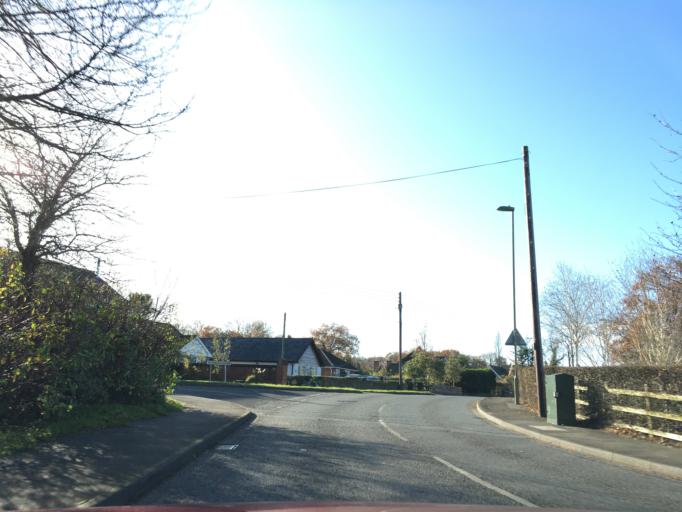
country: GB
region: England
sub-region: Hampshire
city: Colden Common
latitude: 50.9923
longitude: -1.3102
